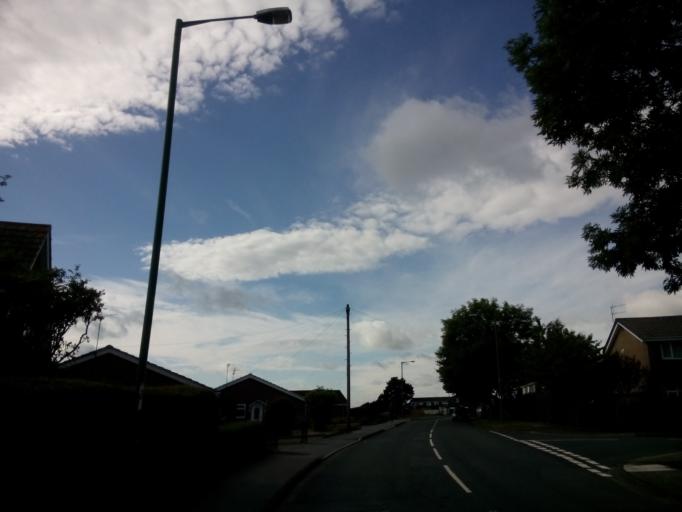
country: GB
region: England
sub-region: County Durham
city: Durham
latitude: 54.8000
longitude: -1.5630
